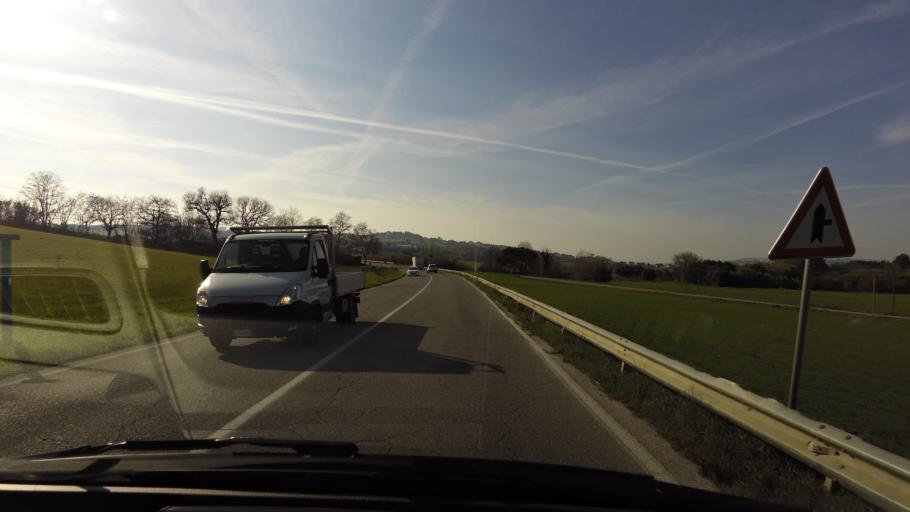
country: IT
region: The Marches
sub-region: Provincia di Ancona
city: Villa Musone
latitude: 43.4767
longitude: 13.5885
